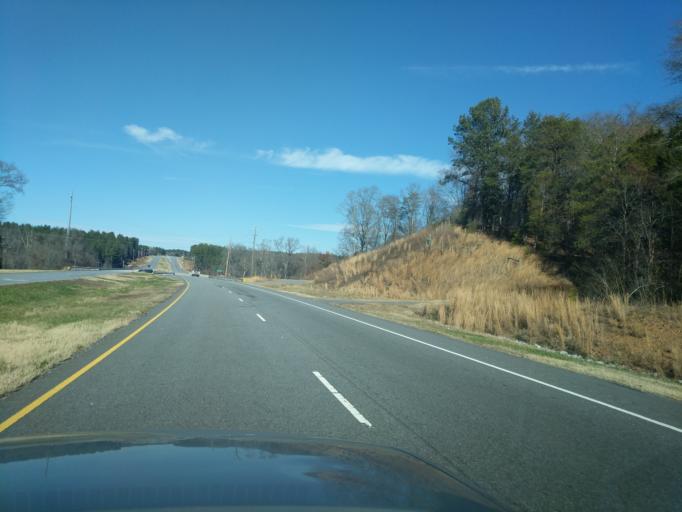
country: US
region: South Carolina
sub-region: Spartanburg County
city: Mayo
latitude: 35.2024
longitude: -81.8375
